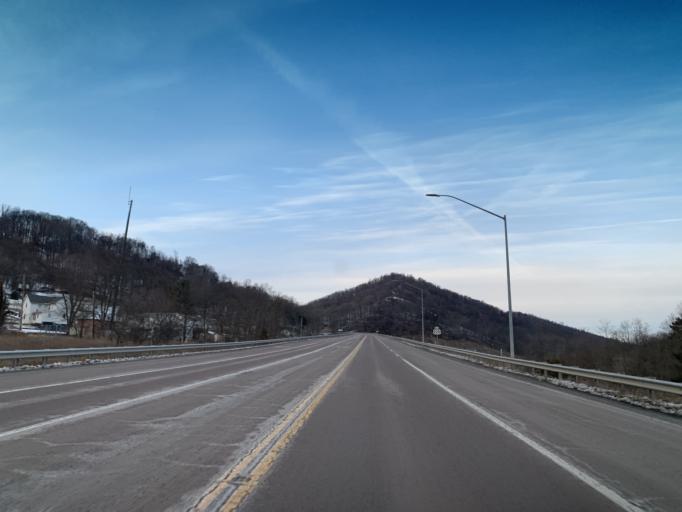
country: US
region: Maryland
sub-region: Allegany County
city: Cumberland
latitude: 39.7155
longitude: -78.7033
